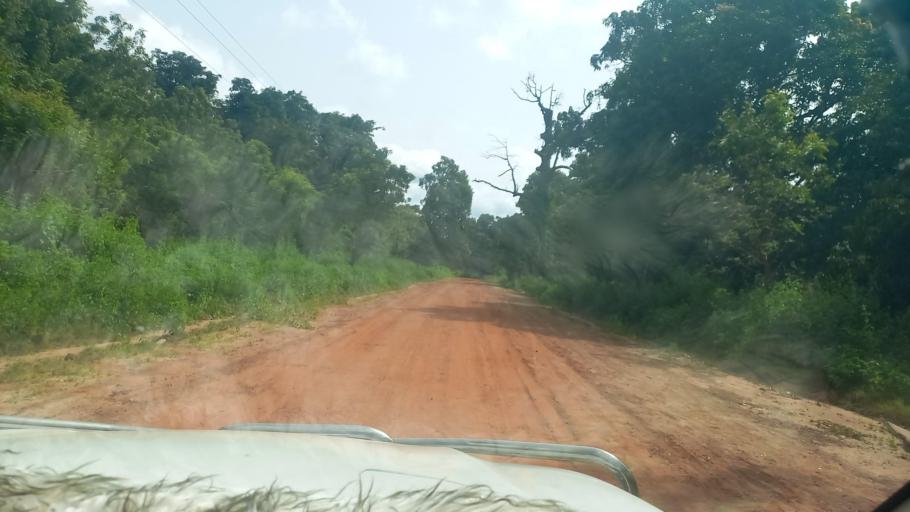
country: SN
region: Ziguinchor
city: Bignona
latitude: 12.7520
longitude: -16.2780
